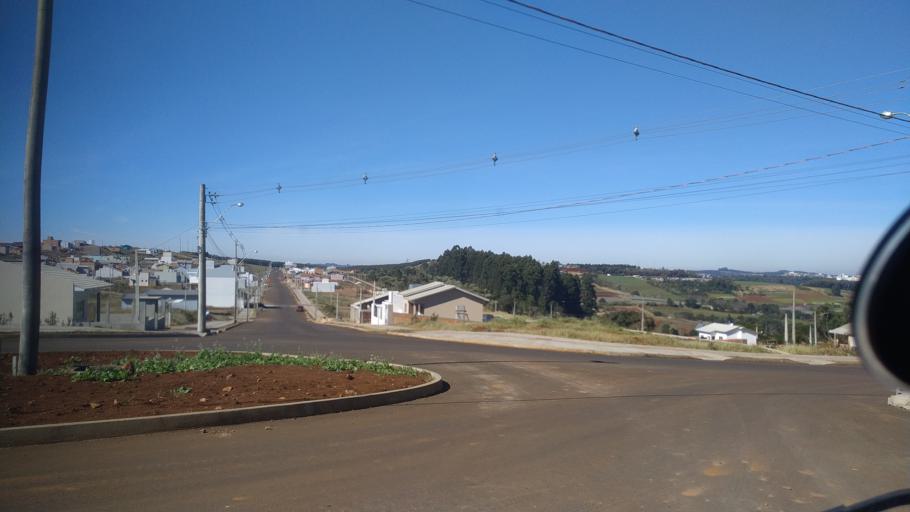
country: BR
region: Santa Catarina
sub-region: Chapeco
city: Chapeco
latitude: -27.0487
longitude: -52.6007
